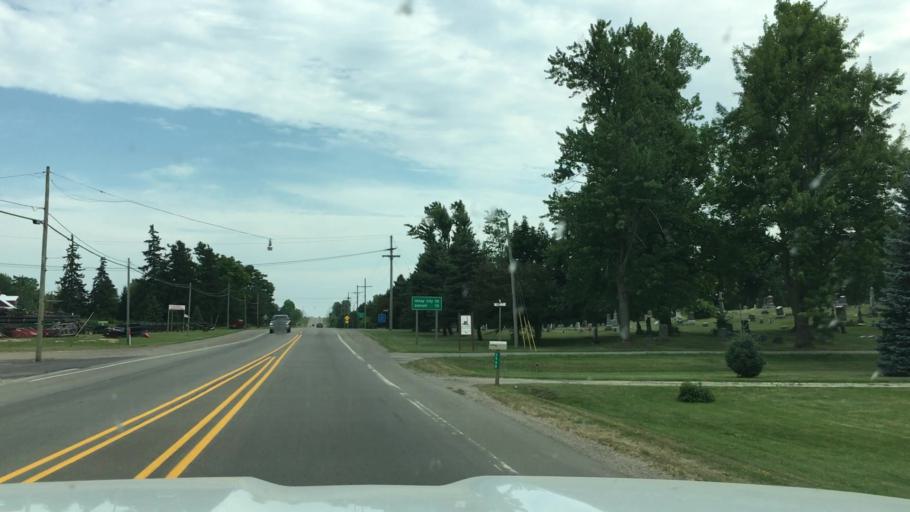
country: US
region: Michigan
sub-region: Sanilac County
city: Marlette
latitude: 43.3161
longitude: -83.0799
